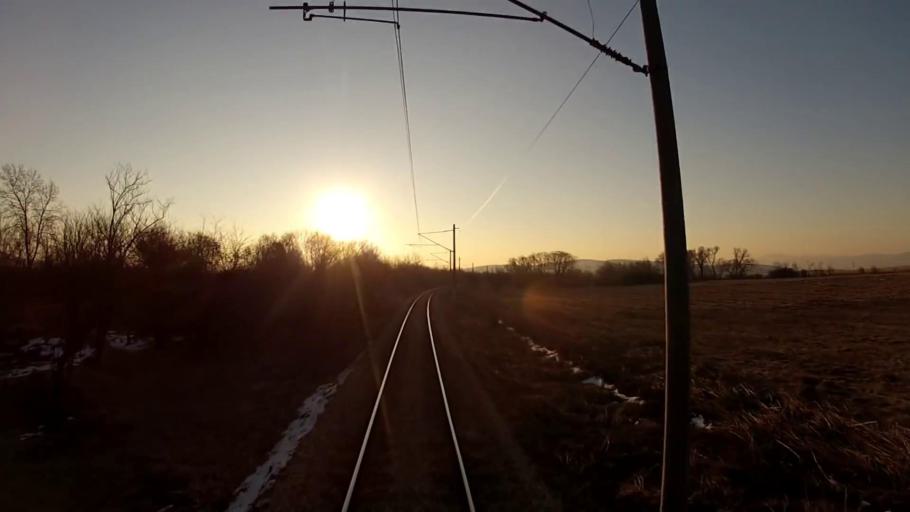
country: BG
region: Sofiya
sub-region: Obshtina Dragoman
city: Dragoman
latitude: 42.8851
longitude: 22.9802
